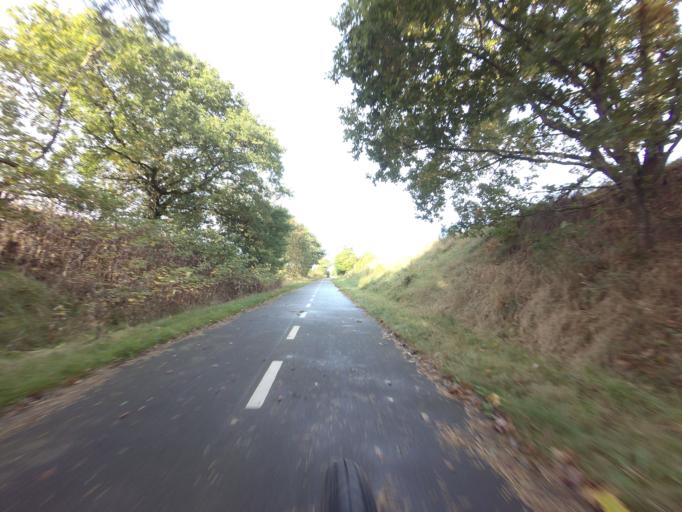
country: DK
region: Central Jutland
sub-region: Viborg Kommune
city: Viborg
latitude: 56.4239
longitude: 9.4307
